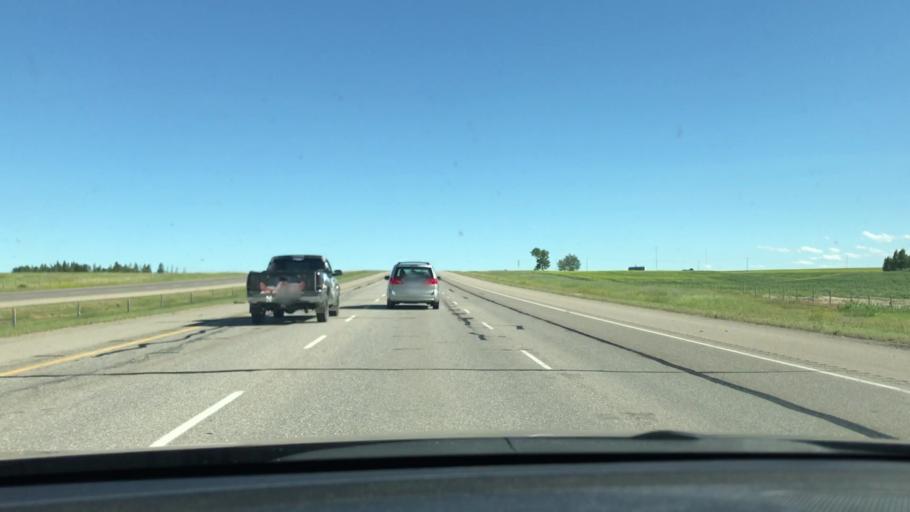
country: CA
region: Alberta
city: Crossfield
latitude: 51.4507
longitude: -114.0155
